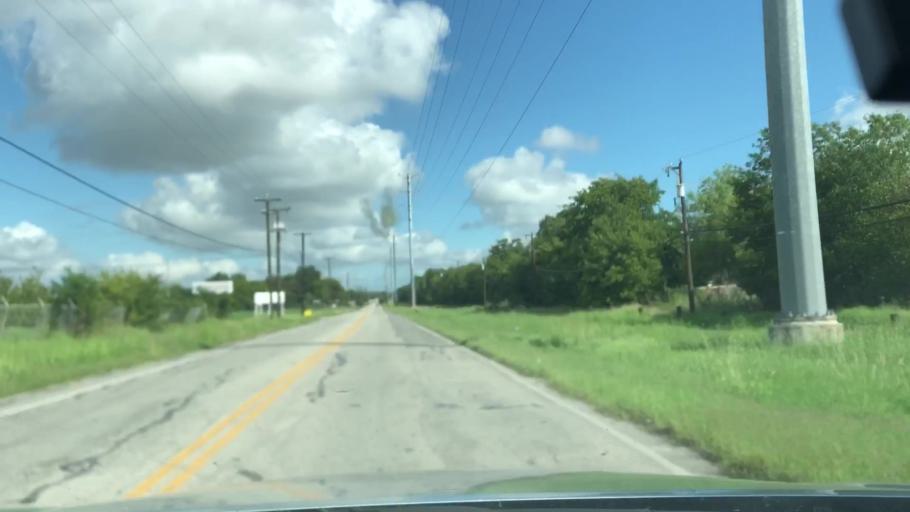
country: US
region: Texas
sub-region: Bexar County
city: Kirby
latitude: 29.4883
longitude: -98.3927
